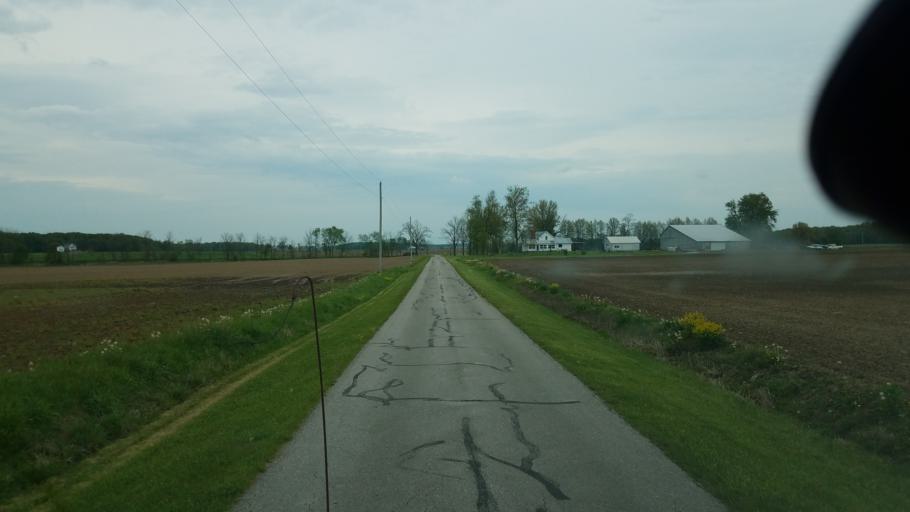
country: US
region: Ohio
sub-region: Huron County
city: Willard
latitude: 41.0122
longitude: -82.8358
